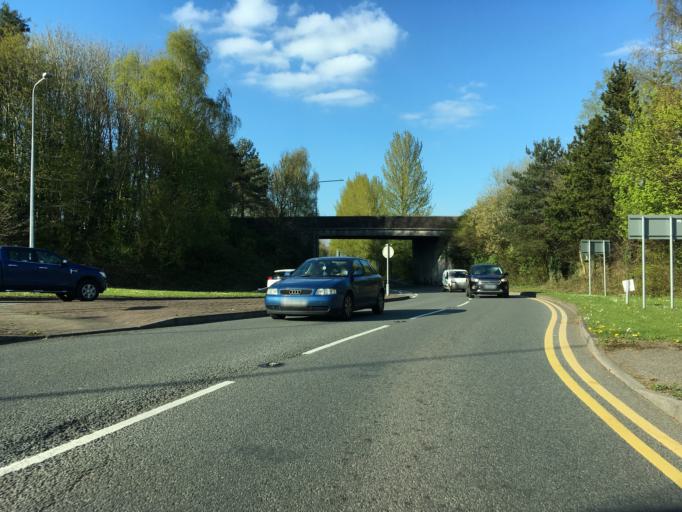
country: GB
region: Wales
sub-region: Torfaen County Borough
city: Cwmbran
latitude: 51.6564
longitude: -3.0263
